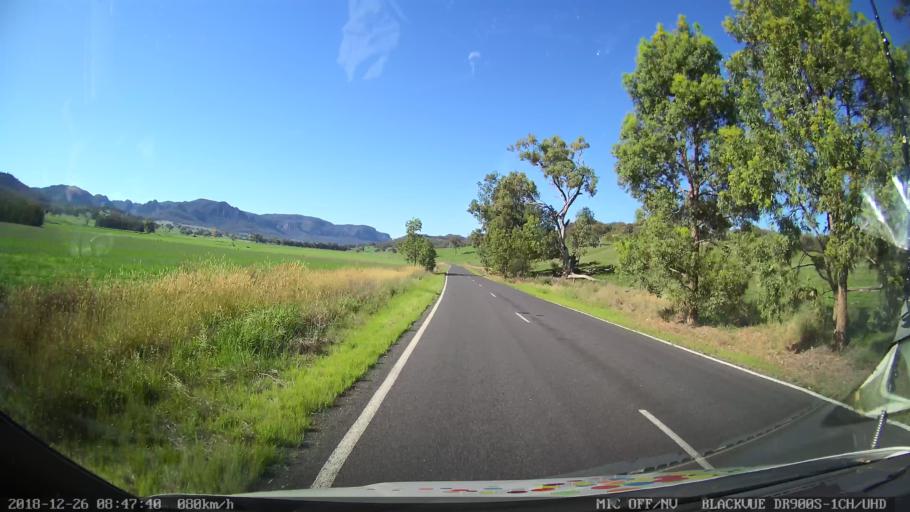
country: AU
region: New South Wales
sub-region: Mid-Western Regional
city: Kandos
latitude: -32.5452
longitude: 150.0900
